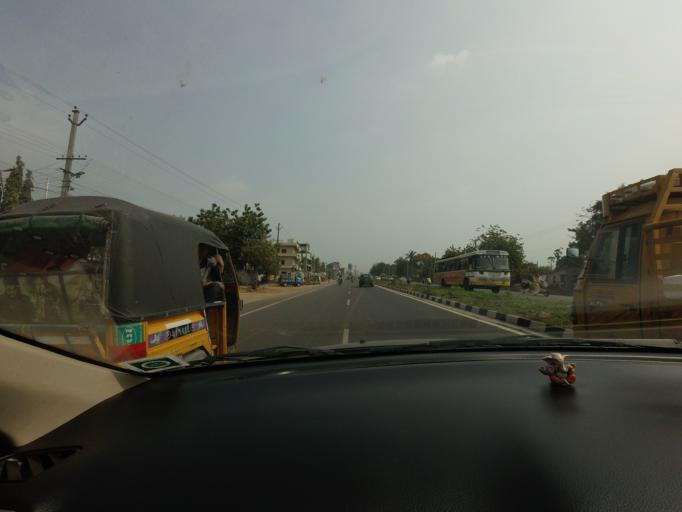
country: IN
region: Andhra Pradesh
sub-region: Krishna
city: Yanamalakuduru
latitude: 16.4817
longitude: 80.6927
